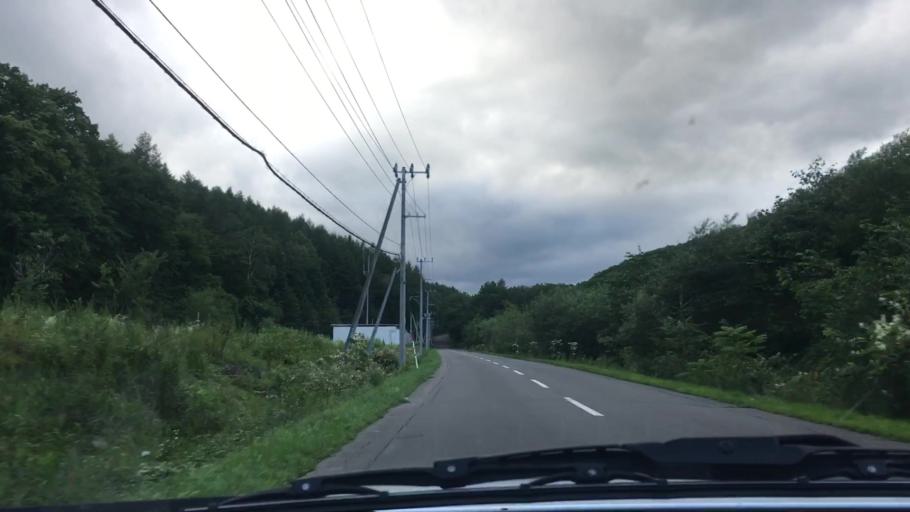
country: JP
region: Hokkaido
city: Otofuke
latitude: 43.1428
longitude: 142.8818
